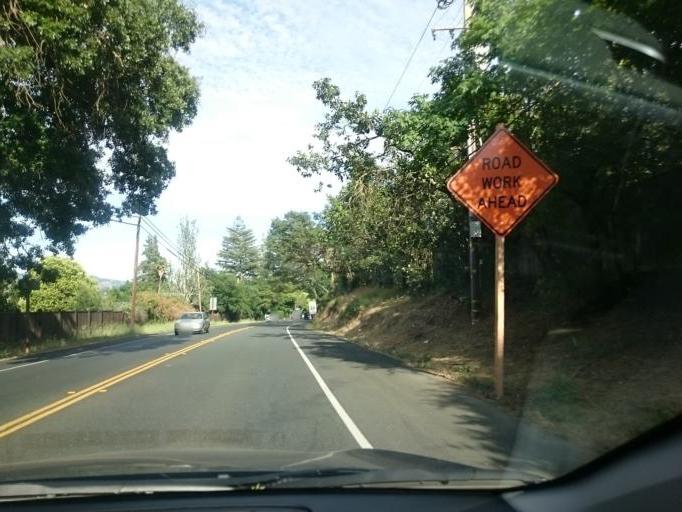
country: US
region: California
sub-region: Napa County
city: Calistoga
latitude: 38.5792
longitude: -122.5913
